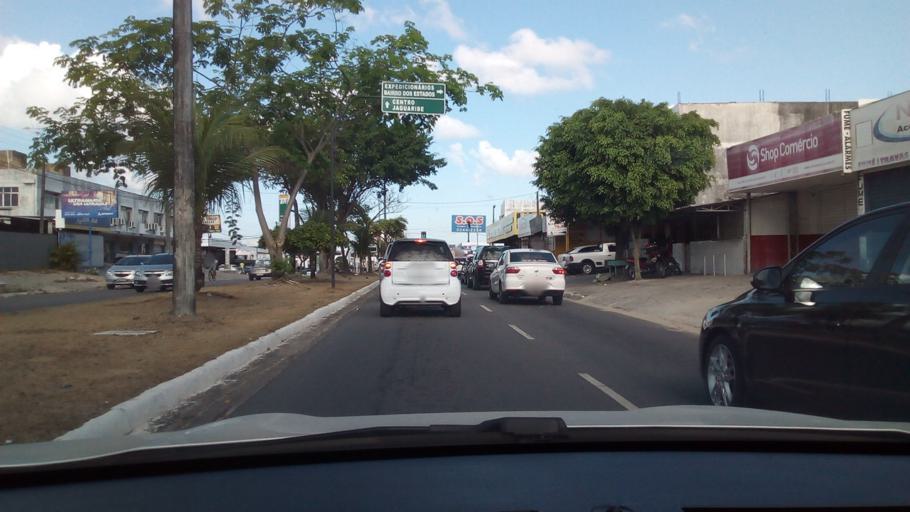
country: BR
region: Paraiba
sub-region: Joao Pessoa
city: Joao Pessoa
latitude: -7.1281
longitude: -34.8602
